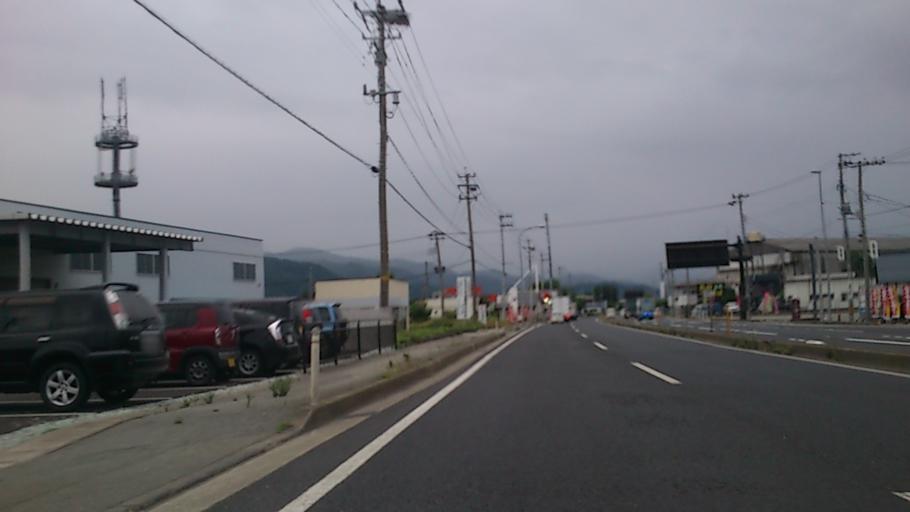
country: JP
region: Yamagata
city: Tendo
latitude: 38.3107
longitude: 140.3634
